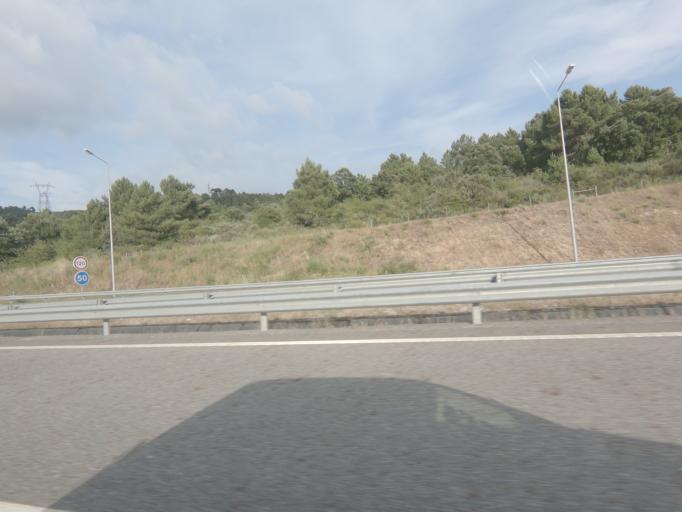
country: PT
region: Vila Real
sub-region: Boticas
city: Boticas
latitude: 41.6717
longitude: -7.5688
